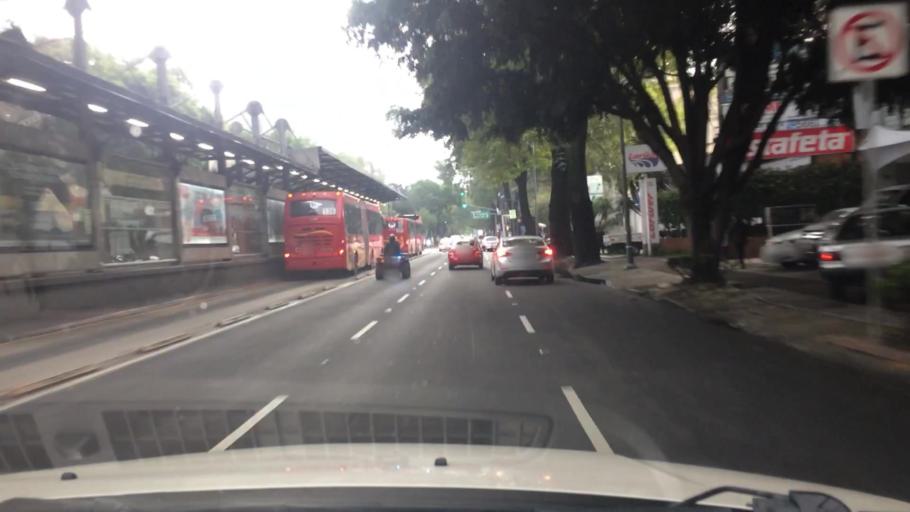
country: MX
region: Mexico City
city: Alvaro Obregon
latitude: 19.3581
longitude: -99.1840
